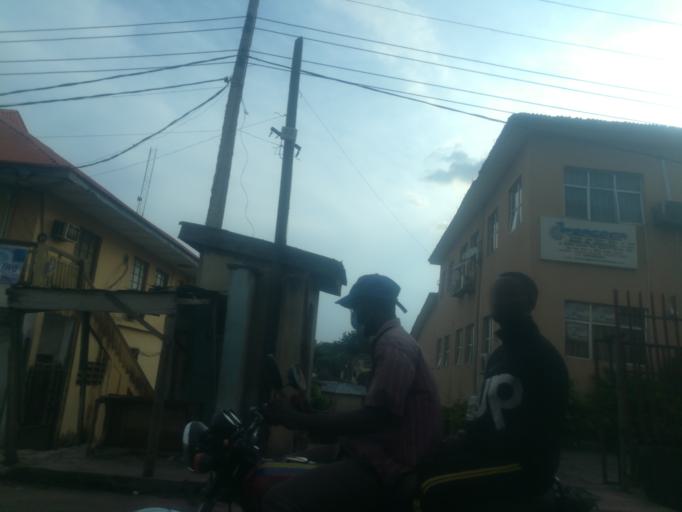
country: NG
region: Oyo
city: Ibadan
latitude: 7.3860
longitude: 3.8800
